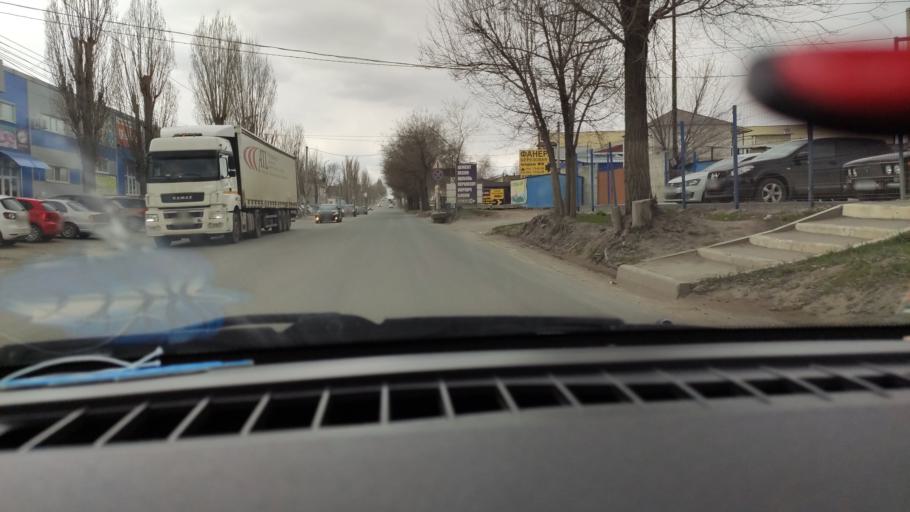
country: RU
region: Saratov
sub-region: Saratovskiy Rayon
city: Saratov
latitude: 51.6151
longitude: 45.9619
